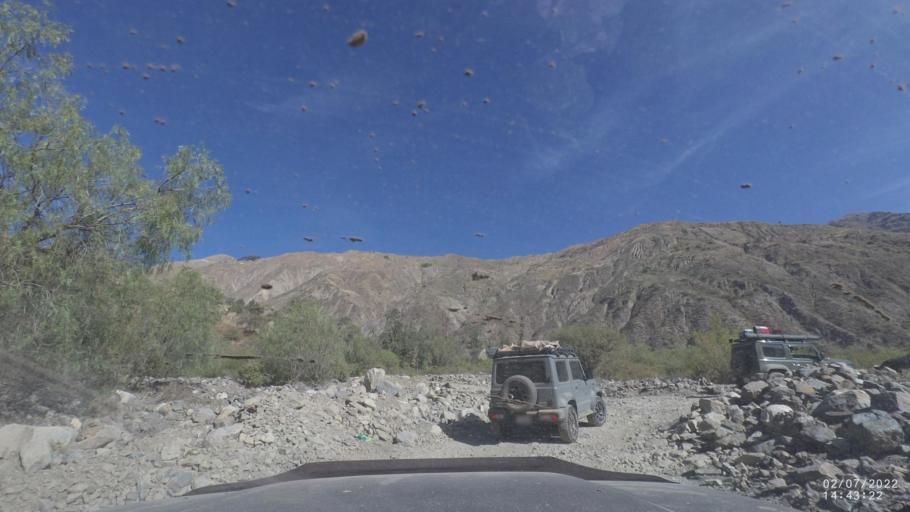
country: BO
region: Cochabamba
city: Irpa Irpa
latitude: -17.8531
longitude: -66.4213
